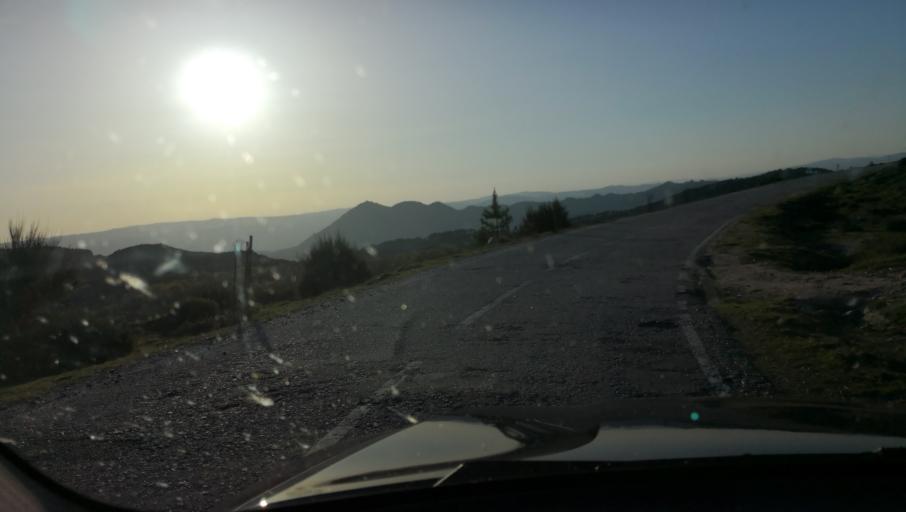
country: PT
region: Vila Real
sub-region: Vila Real
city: Vila Real
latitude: 41.3877
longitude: -7.8263
